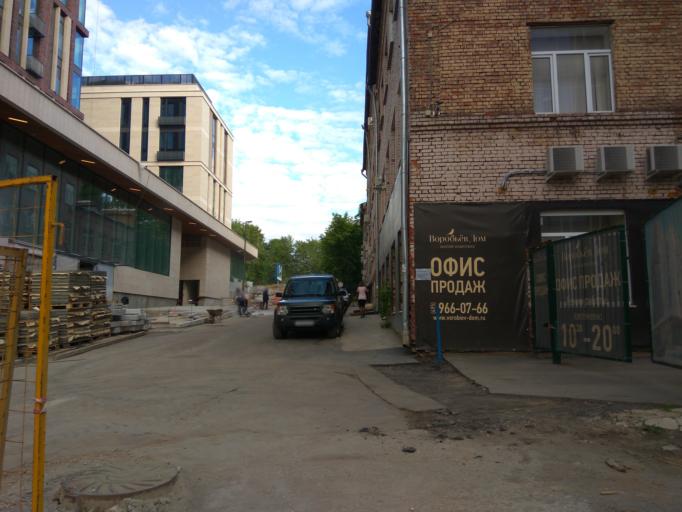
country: RU
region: Moscow
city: Vorob'yovo
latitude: 55.7278
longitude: 37.5347
